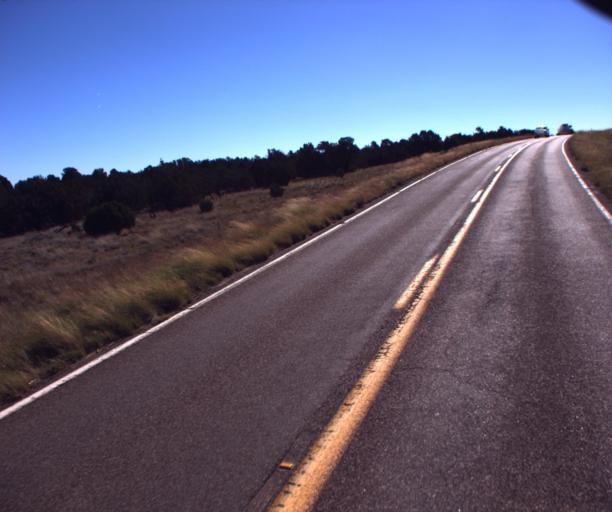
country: US
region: Arizona
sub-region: Navajo County
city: Heber-Overgaard
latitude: 34.4584
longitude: -110.4665
